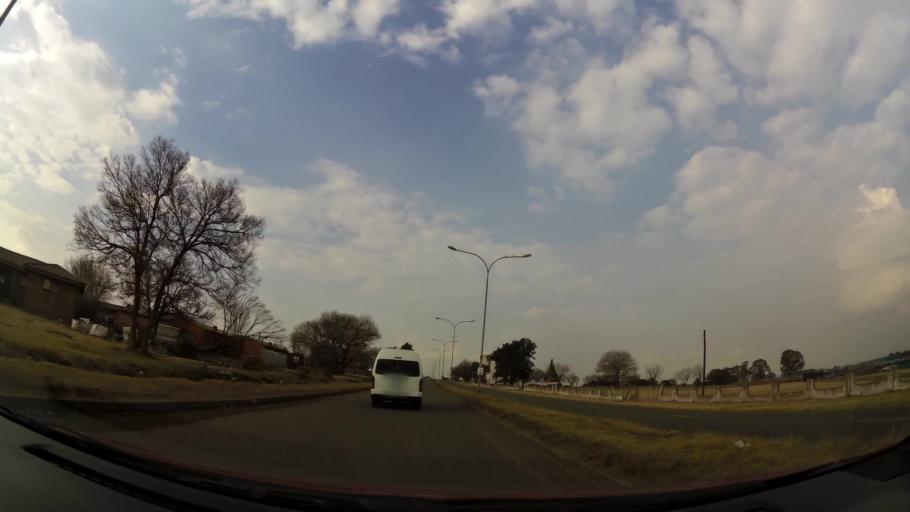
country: ZA
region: Gauteng
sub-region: Sedibeng District Municipality
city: Vereeniging
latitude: -26.6781
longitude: 27.8887
